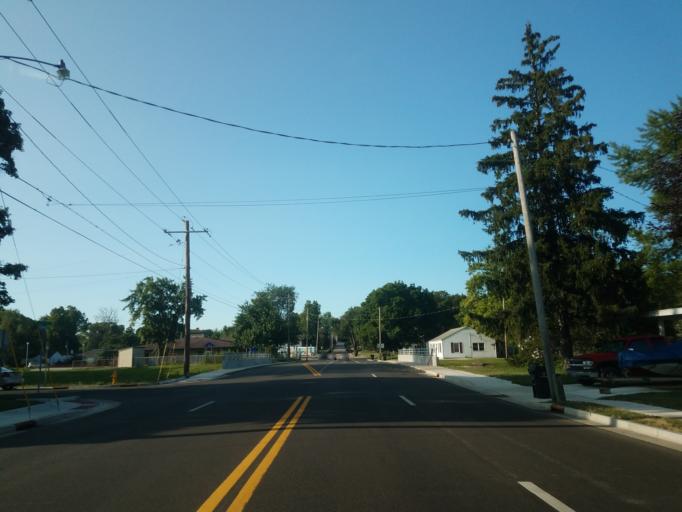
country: US
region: Illinois
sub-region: McLean County
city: Bloomington
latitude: 40.4946
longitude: -88.9820
